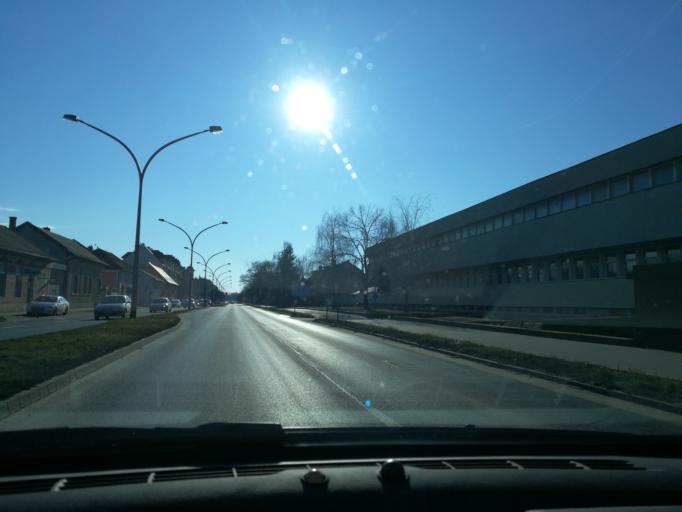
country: HU
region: Szabolcs-Szatmar-Bereg
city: Nyiregyhaza
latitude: 47.9538
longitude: 21.7041
